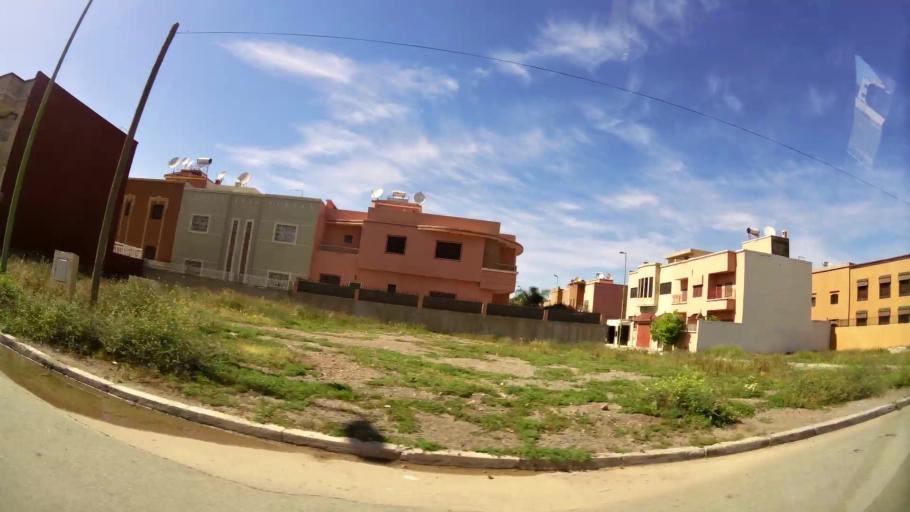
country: MA
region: Marrakech-Tensift-Al Haouz
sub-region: Marrakech
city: Marrakesh
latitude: 31.6359
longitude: -8.0388
